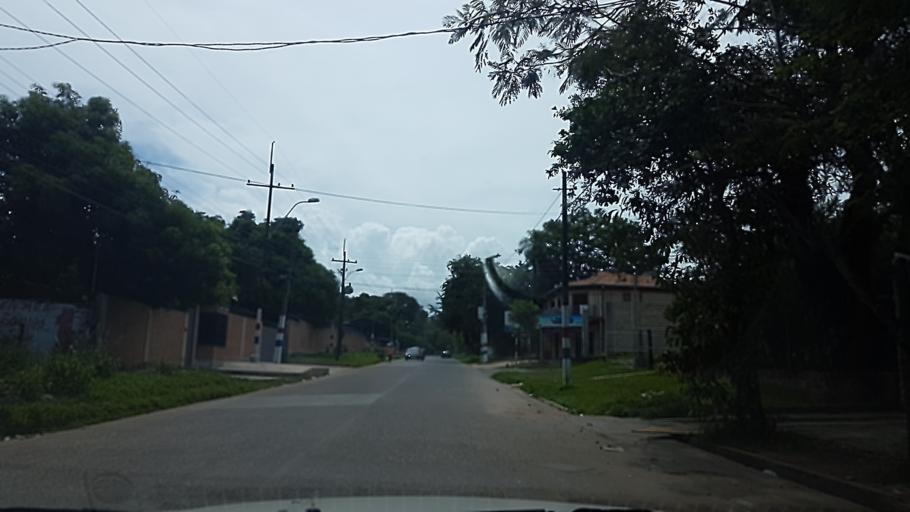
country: PY
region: Central
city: Colonia Mariano Roque Alonso
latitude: -25.1998
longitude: -57.5339
